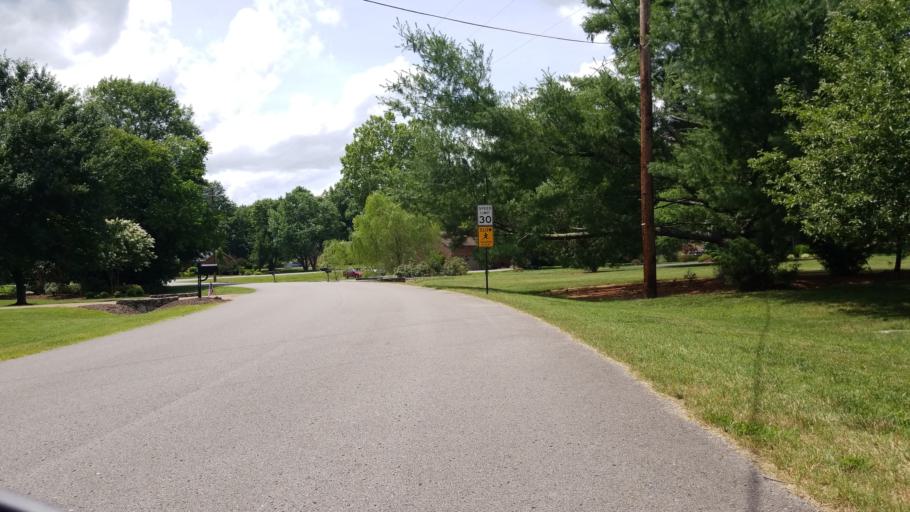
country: US
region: Tennessee
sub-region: Davidson County
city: Forest Hills
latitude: 36.0392
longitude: -86.8434
